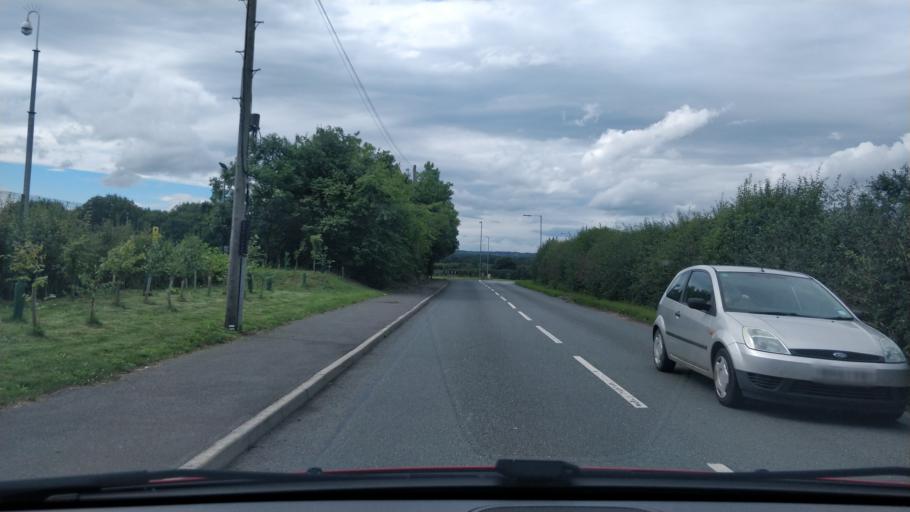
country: GB
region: England
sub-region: Cheshire West and Chester
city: Eccleston
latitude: 53.1551
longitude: -2.9274
